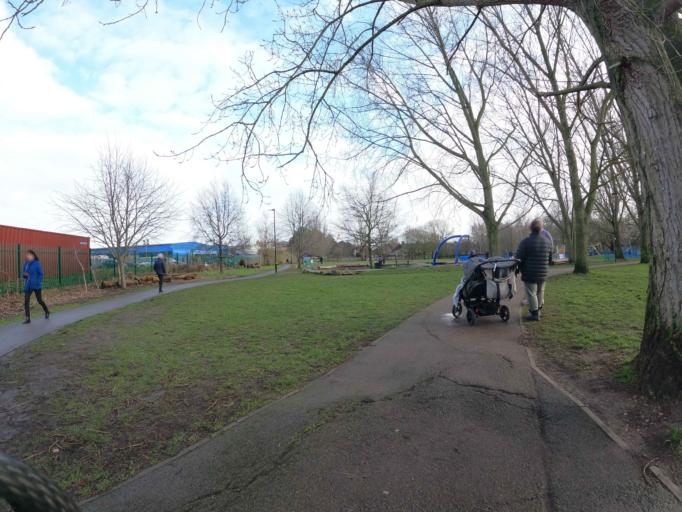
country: GB
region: England
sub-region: Greater London
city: Acton
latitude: 51.5046
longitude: -0.2616
